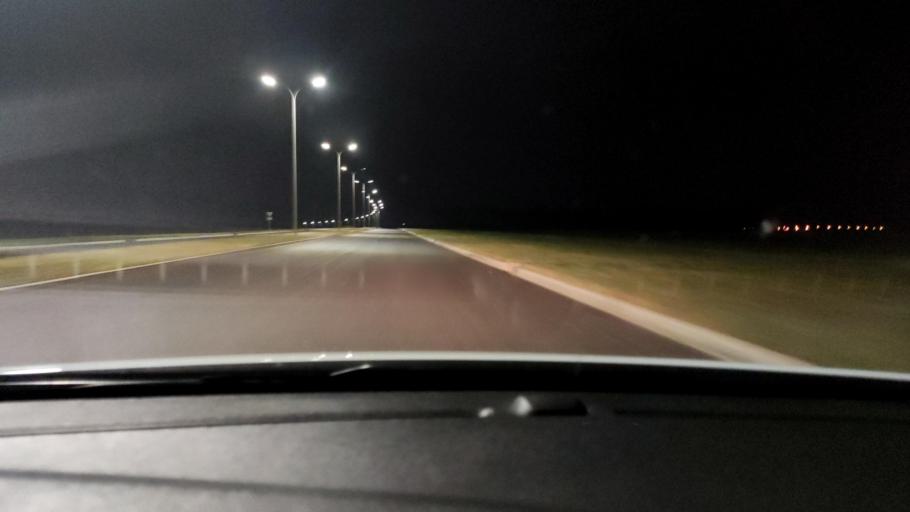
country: RU
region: Tatarstan
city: Sviyazhsk
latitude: 55.7381
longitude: 48.7379
